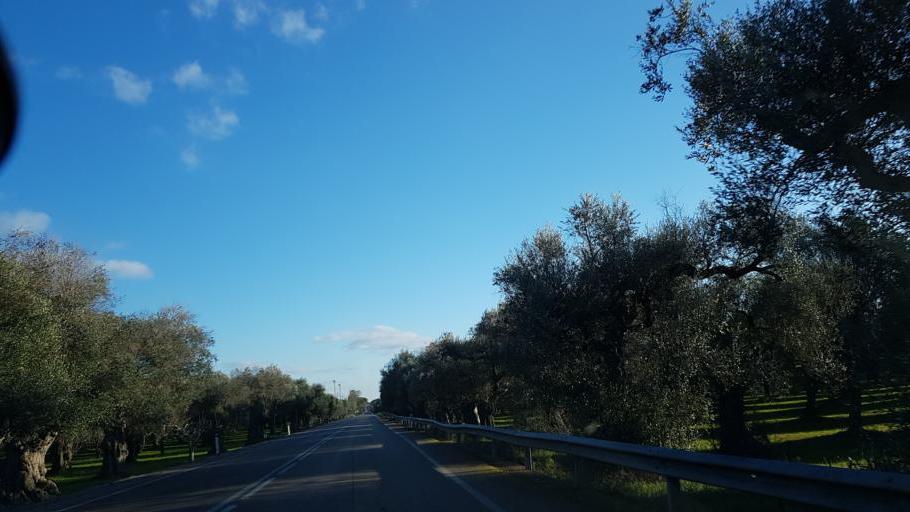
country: IT
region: Apulia
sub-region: Provincia di Lecce
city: Squinzano
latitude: 40.4498
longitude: 18.0291
